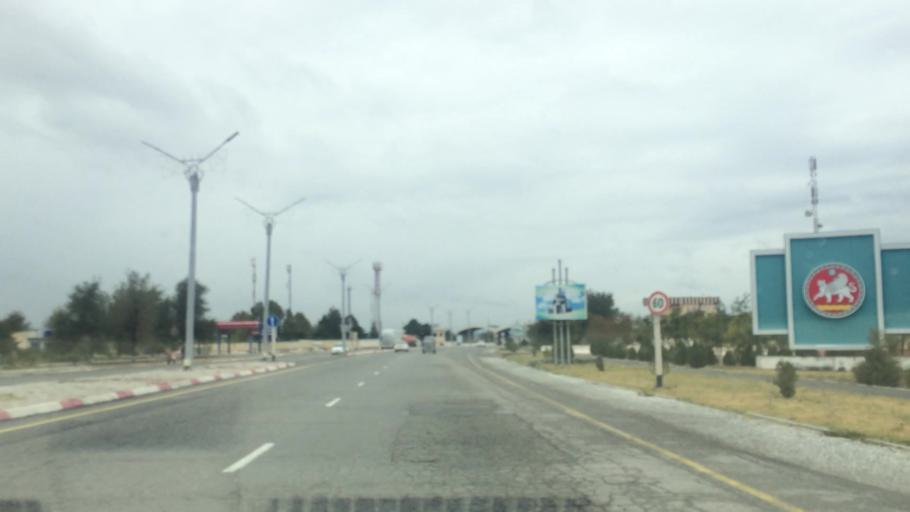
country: UZ
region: Samarqand
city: Bulung'ur
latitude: 39.8517
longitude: 67.4631
